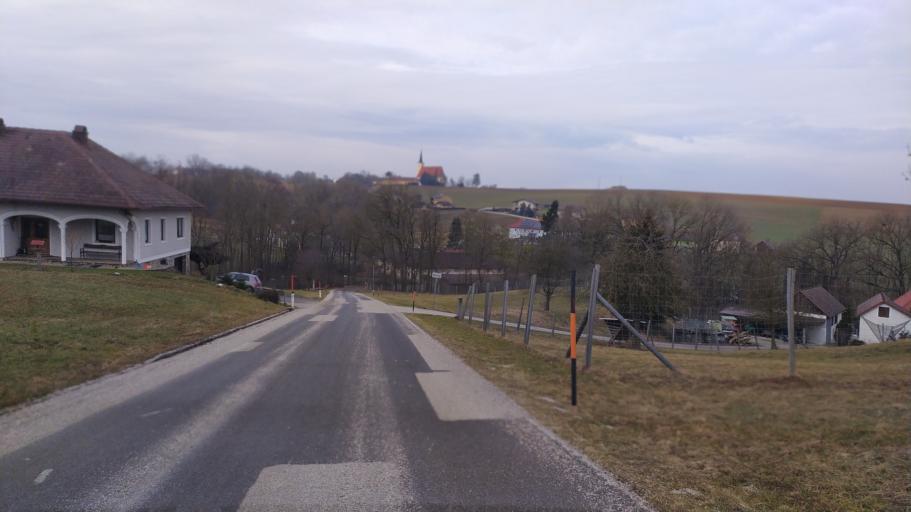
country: AT
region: Lower Austria
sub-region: Politischer Bezirk Amstetten
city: Zeillern
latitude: 48.1517
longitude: 14.7245
